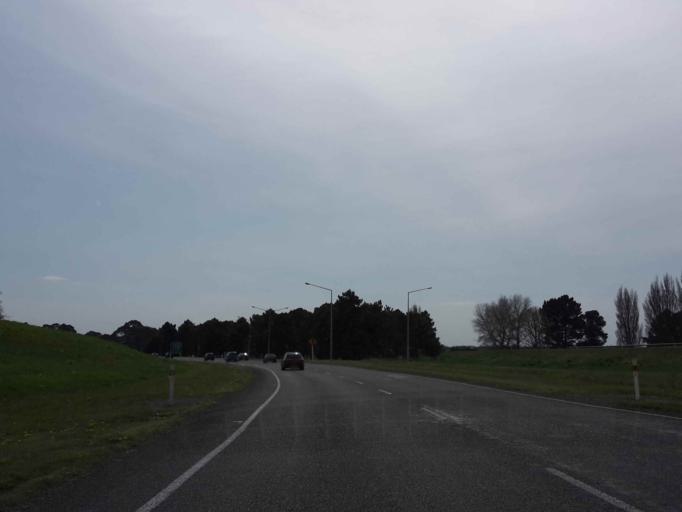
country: NZ
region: Canterbury
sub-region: Waimakariri District
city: Kaiapoi
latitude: -43.4293
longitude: 172.6454
